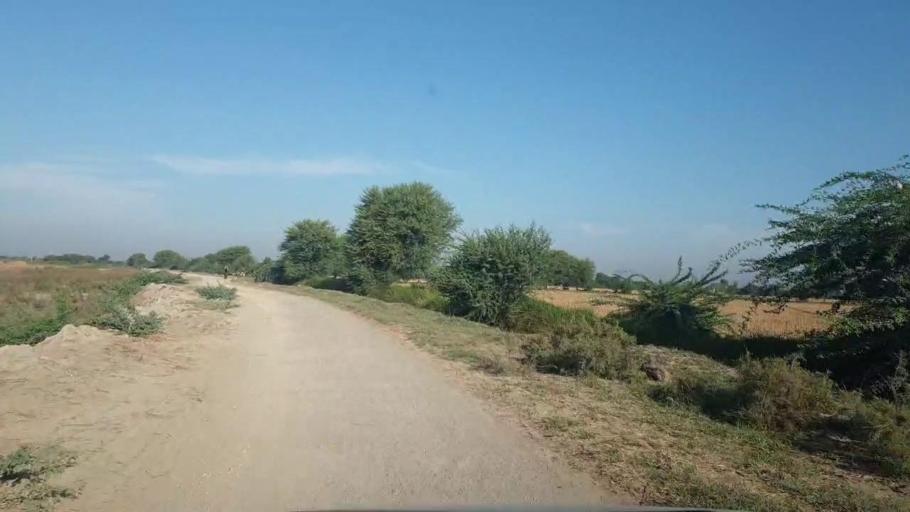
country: PK
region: Sindh
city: Talhar
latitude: 24.8238
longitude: 68.8233
